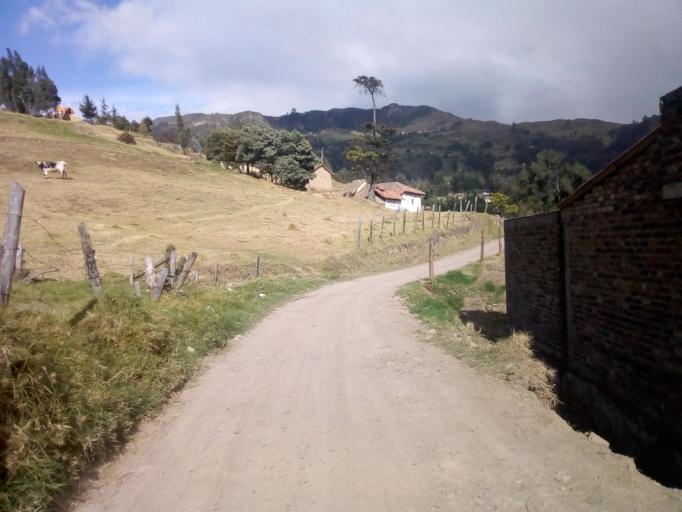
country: CO
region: Boyaca
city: Gameza
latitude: 5.8052
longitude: -72.8059
